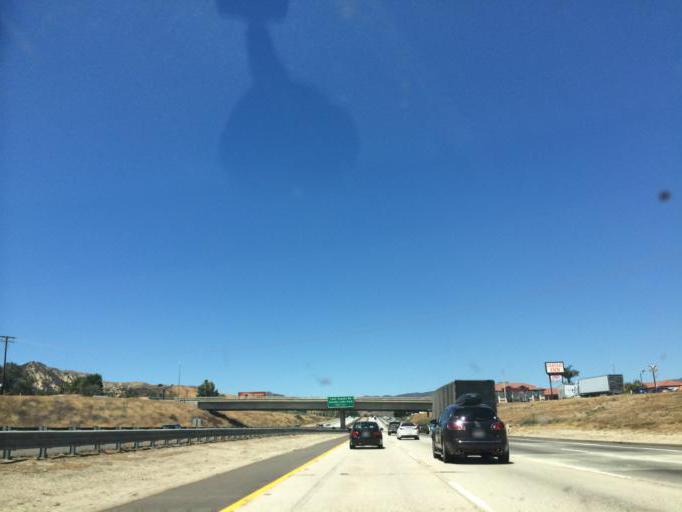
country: US
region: California
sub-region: Los Angeles County
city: Castaic
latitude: 34.4884
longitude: -118.6182
